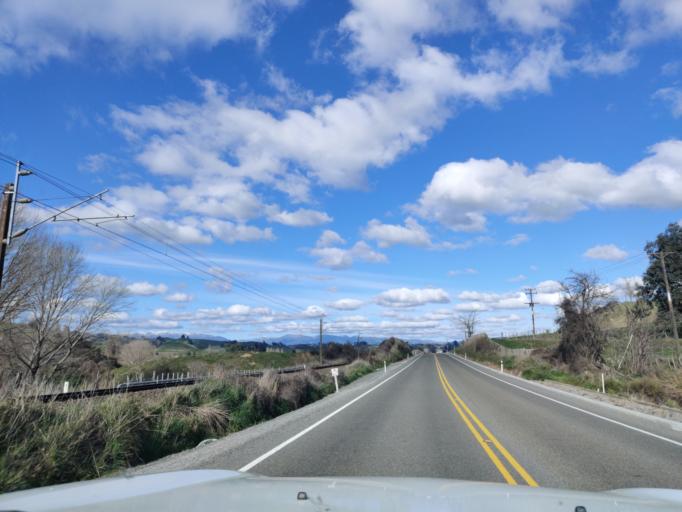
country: NZ
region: Manawatu-Wanganui
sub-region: Ruapehu District
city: Waiouru
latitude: -39.7048
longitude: 175.8317
